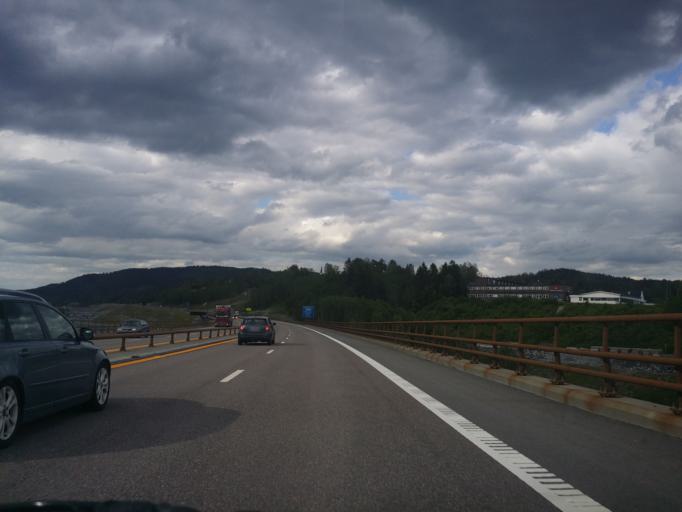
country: NO
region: Akershus
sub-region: Eidsvoll
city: Eidsvoll
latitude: 60.4003
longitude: 11.2338
